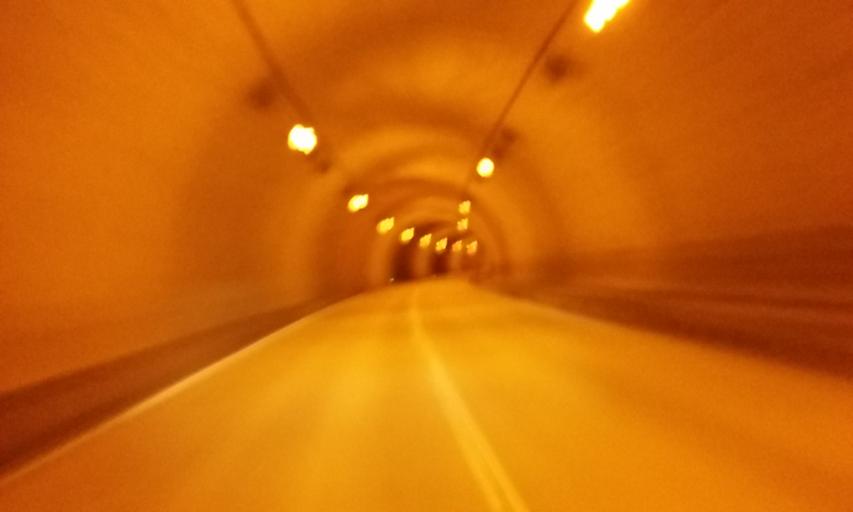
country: JP
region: Ehime
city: Saijo
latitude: 33.8480
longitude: 133.2123
